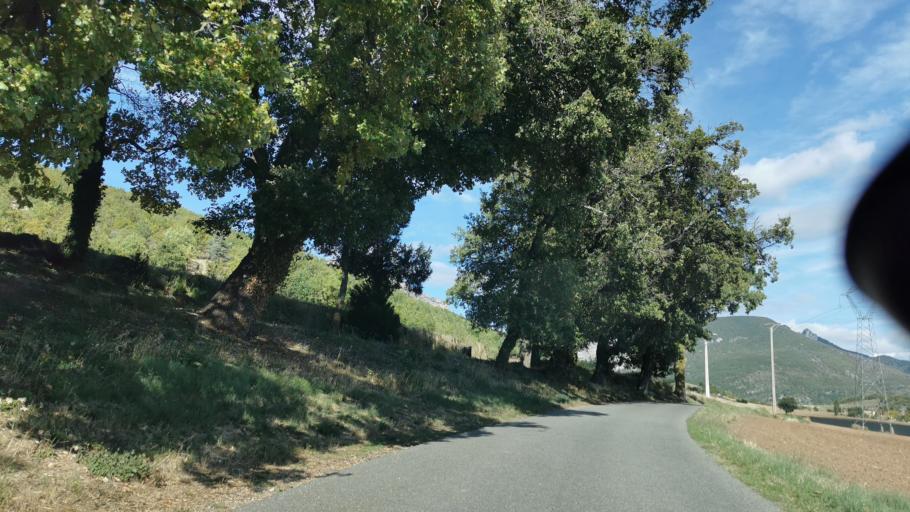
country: FR
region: Provence-Alpes-Cote d'Azur
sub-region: Departement des Alpes-de-Haute-Provence
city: Sisteron
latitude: 44.1744
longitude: 5.9713
